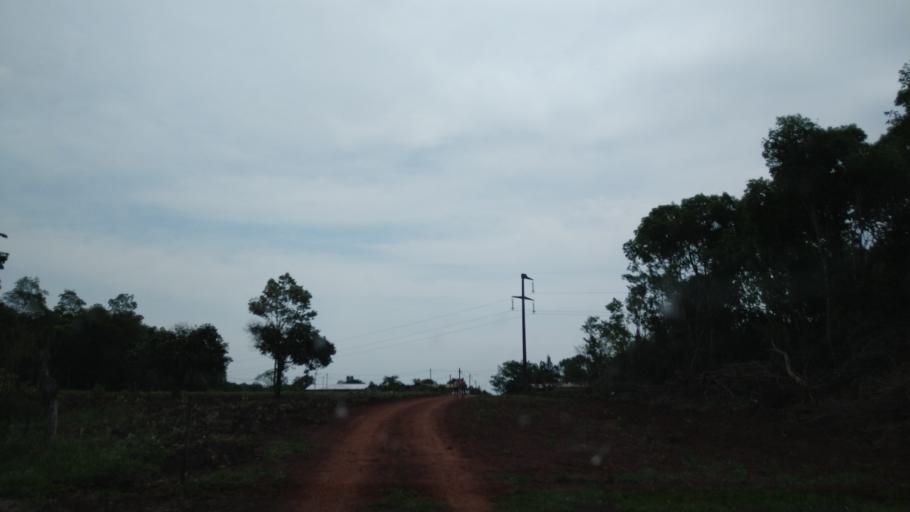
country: AR
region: Misiones
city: Capiovi
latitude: -26.9304
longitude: -55.0483
